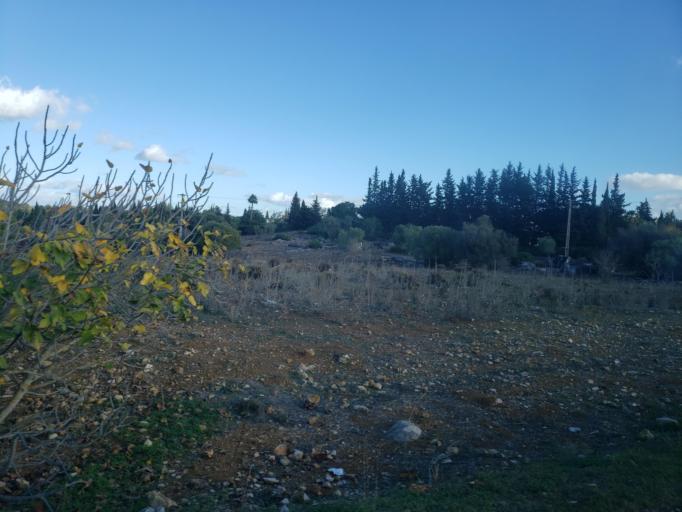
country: PT
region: Faro
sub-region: Portimao
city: Alvor
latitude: 37.1891
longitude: -8.5876
